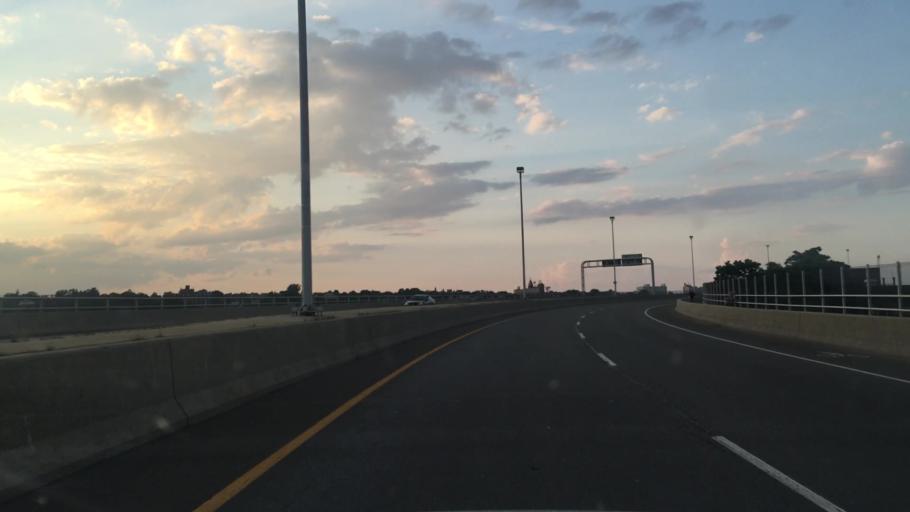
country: US
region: Maine
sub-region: Cumberland County
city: South Portland
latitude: 43.6372
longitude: -70.2588
